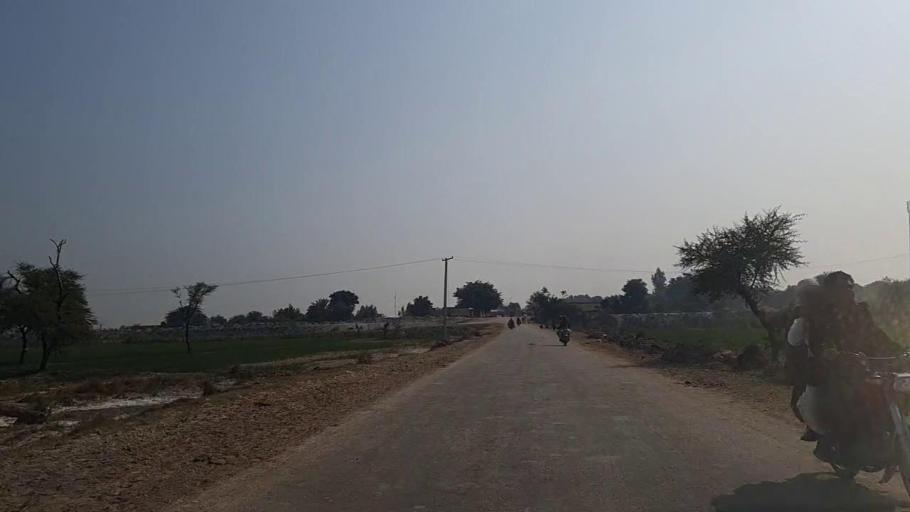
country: PK
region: Sindh
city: Jam Sahib
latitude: 26.3343
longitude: 68.5364
